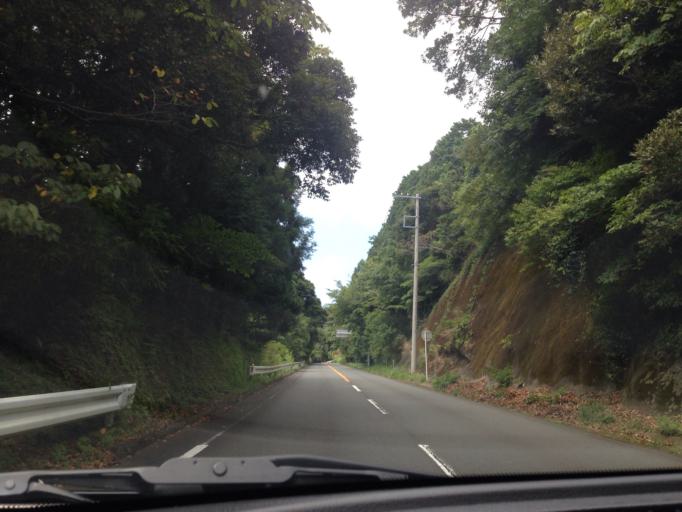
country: JP
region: Shizuoka
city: Shimoda
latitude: 34.7047
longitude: 138.7587
